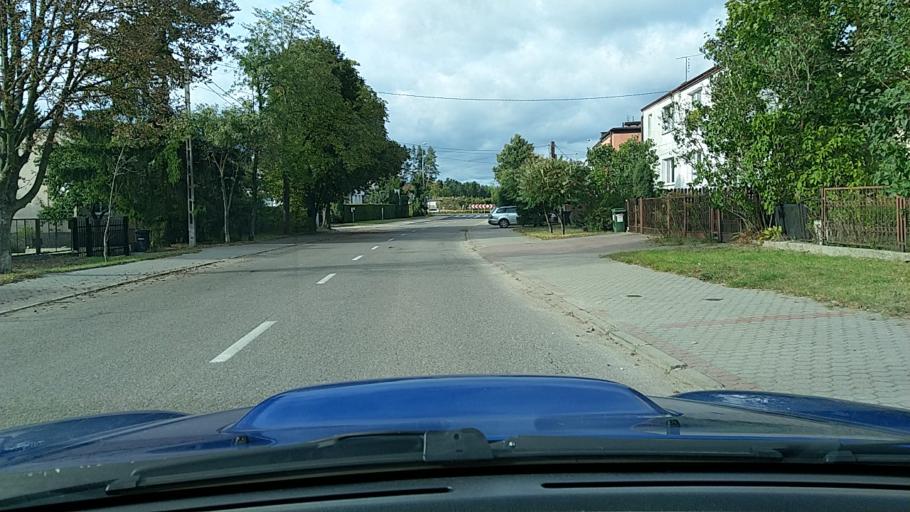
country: PL
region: Warmian-Masurian Voivodeship
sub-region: Olsztyn
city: Kortowo
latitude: 53.7684
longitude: 20.4350
